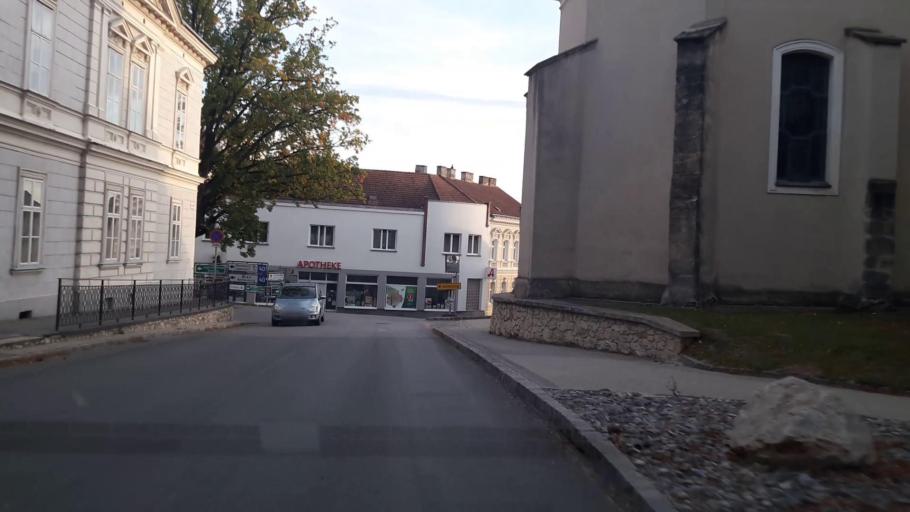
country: AT
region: Lower Austria
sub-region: Politischer Bezirk Korneuburg
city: Ernstbrunn
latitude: 48.5281
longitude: 16.3609
